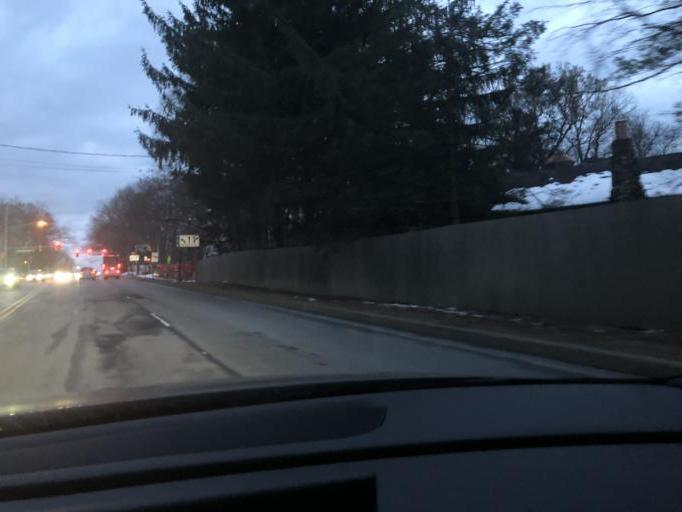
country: US
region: New Jersey
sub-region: Morris County
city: Morristown
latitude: 40.7950
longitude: -74.4495
